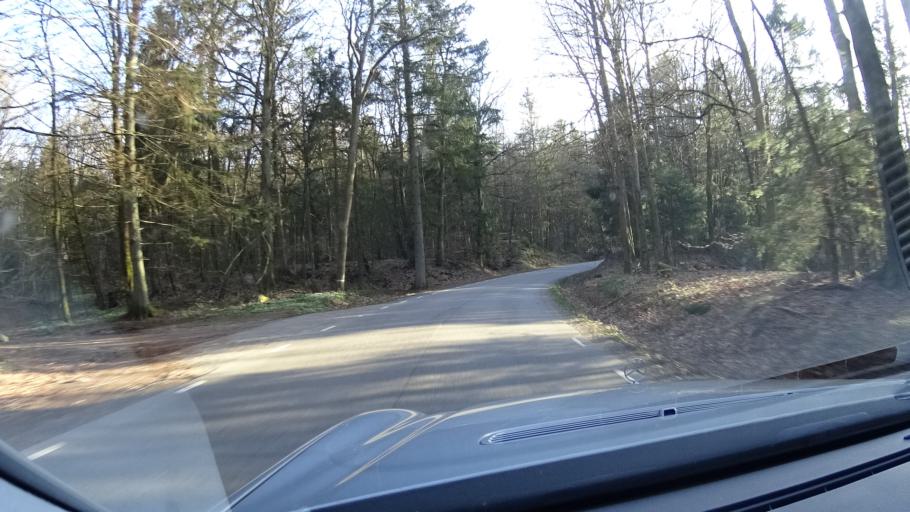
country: SE
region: Skane
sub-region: Hoors Kommun
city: Hoeoer
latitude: 55.9150
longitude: 13.4992
